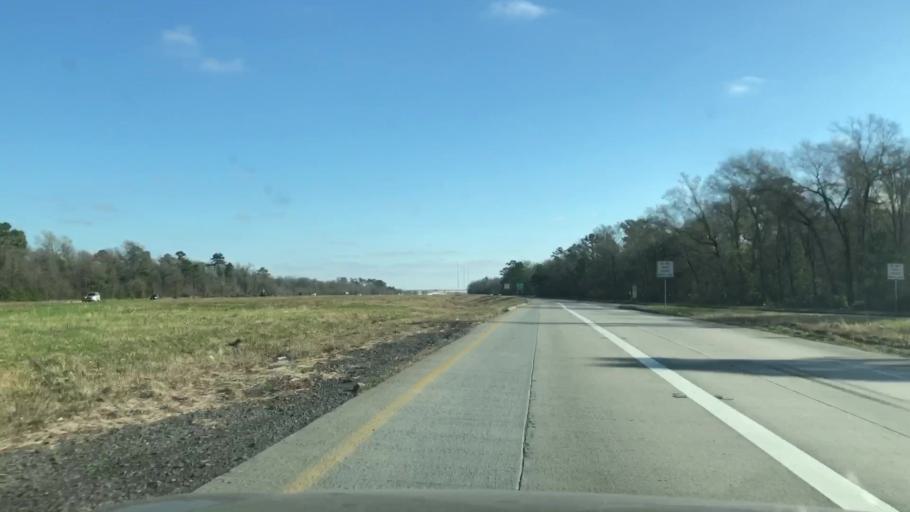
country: US
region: Texas
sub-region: Harris County
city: Cloverleaf
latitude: 29.8211
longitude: -95.2009
